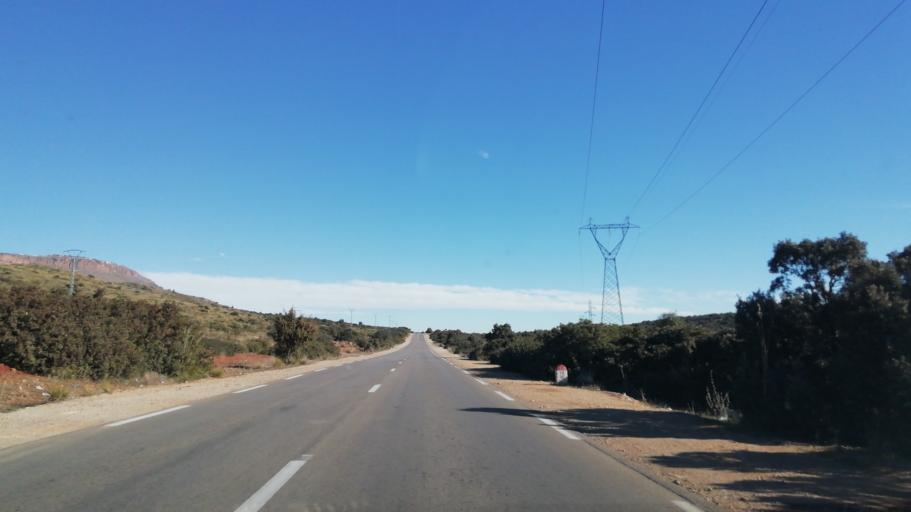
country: DZ
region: Tlemcen
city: Sebdou
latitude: 34.7159
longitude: -1.2051
